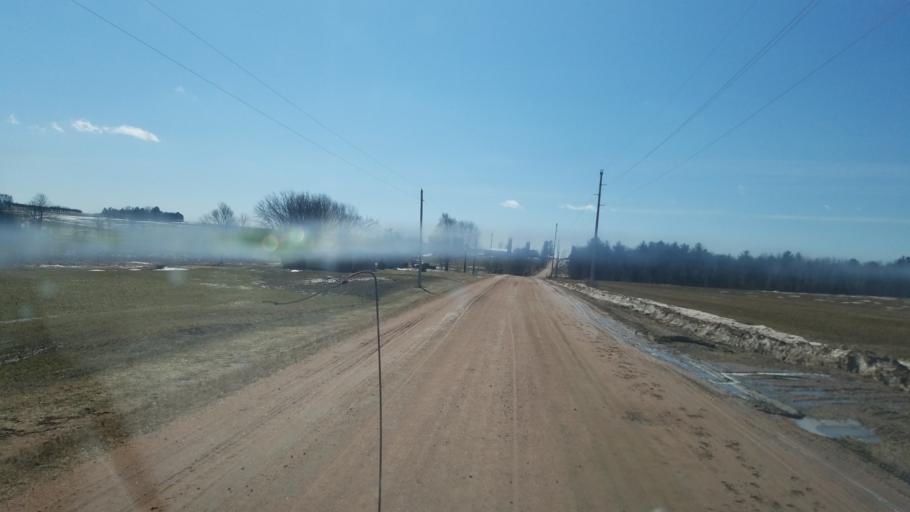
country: US
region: Wisconsin
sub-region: Clark County
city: Loyal
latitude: 44.5888
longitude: -90.3956
